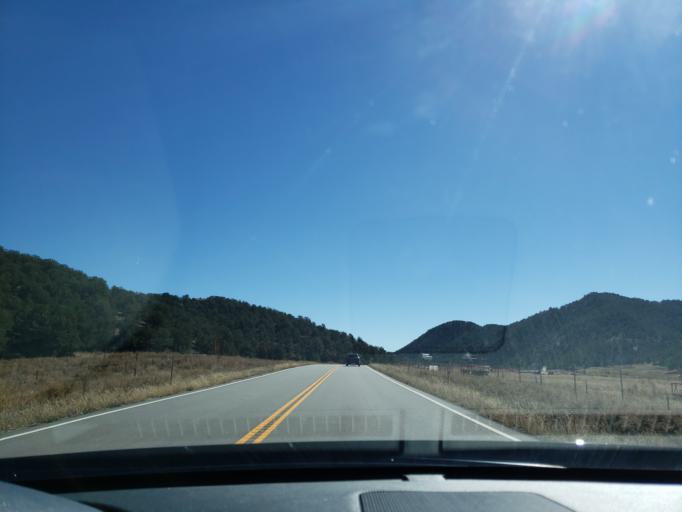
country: US
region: Colorado
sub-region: Fremont County
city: Canon City
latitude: 38.6291
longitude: -105.4599
